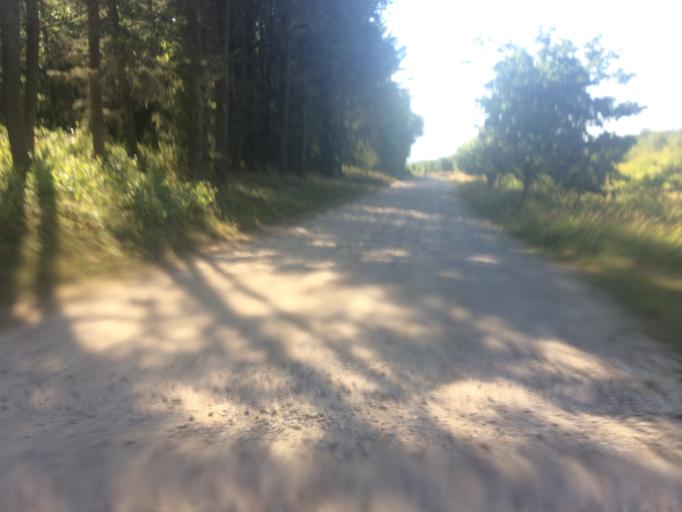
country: DK
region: Central Jutland
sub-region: Holstebro Kommune
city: Vinderup
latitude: 56.5784
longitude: 8.7248
